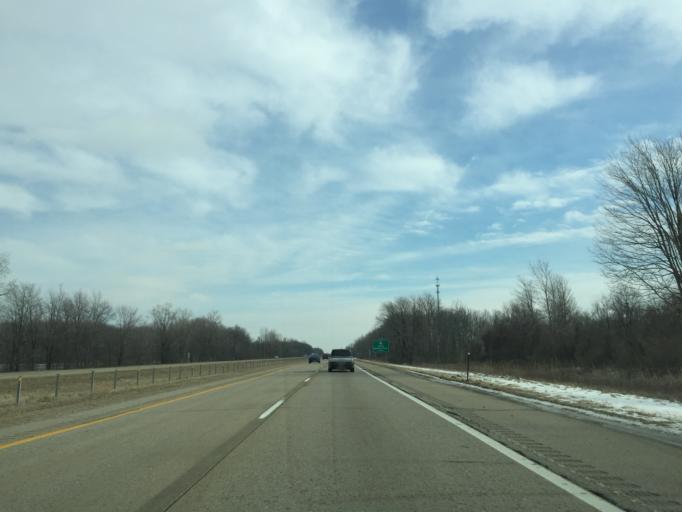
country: US
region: Michigan
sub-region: Ionia County
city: Lake Odessa
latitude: 42.8792
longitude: -85.1043
